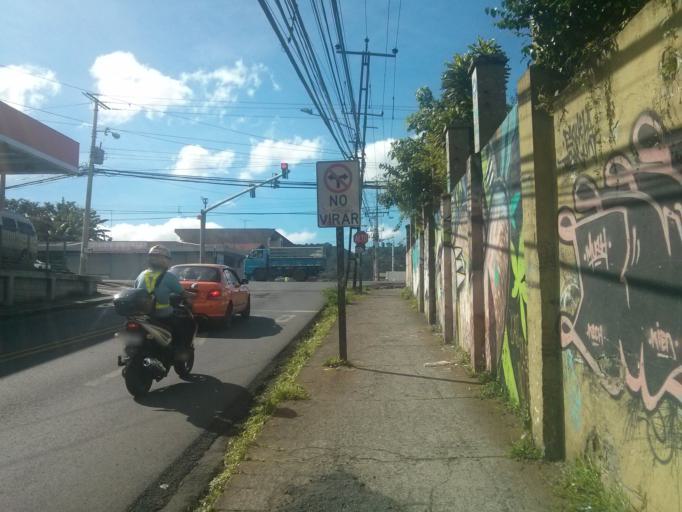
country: CR
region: San Jose
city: Curridabat
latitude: 9.9158
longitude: -84.0340
